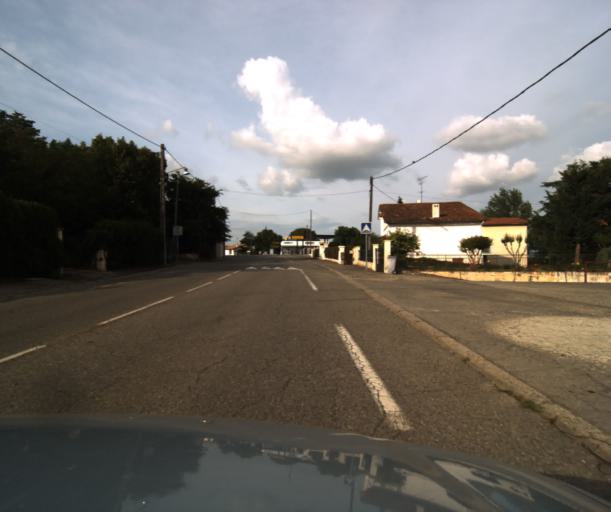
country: FR
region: Midi-Pyrenees
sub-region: Departement du Tarn-et-Garonne
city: Beaumont-de-Lomagne
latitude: 43.8799
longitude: 0.9832
